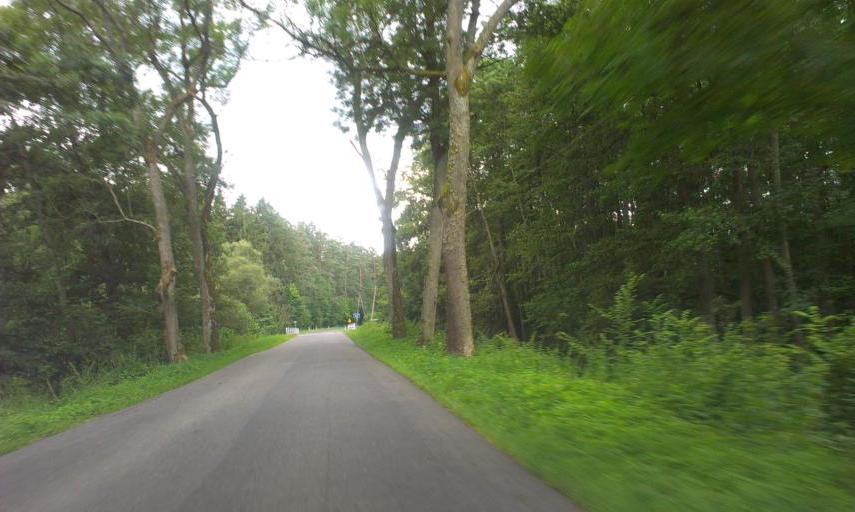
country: PL
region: West Pomeranian Voivodeship
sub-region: Powiat bialogardzki
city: Tychowo
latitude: 53.8739
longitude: 16.1770
